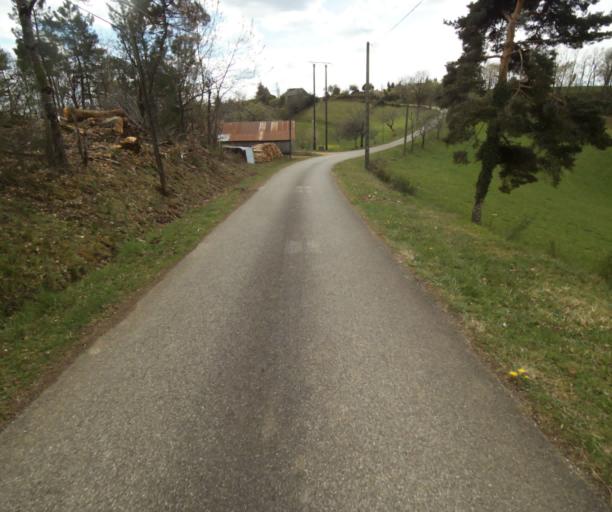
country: FR
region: Limousin
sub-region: Departement de la Correze
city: Sainte-Fortunade
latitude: 45.1921
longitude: 1.8556
